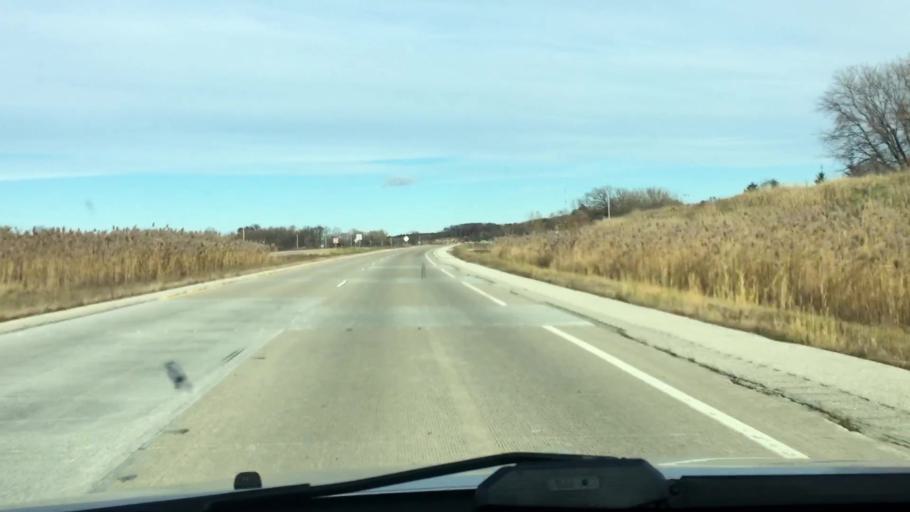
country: US
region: Wisconsin
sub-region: Kewaunee County
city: Luxemburg
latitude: 44.6724
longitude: -87.7371
